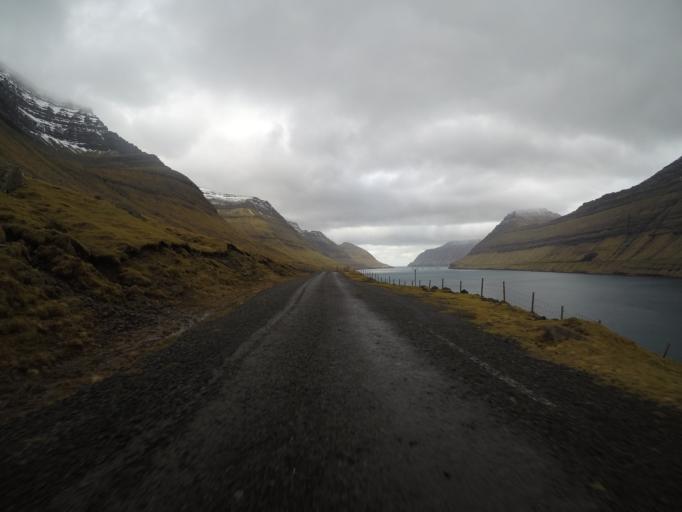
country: FO
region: Nordoyar
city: Klaksvik
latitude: 62.3087
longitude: -6.5432
